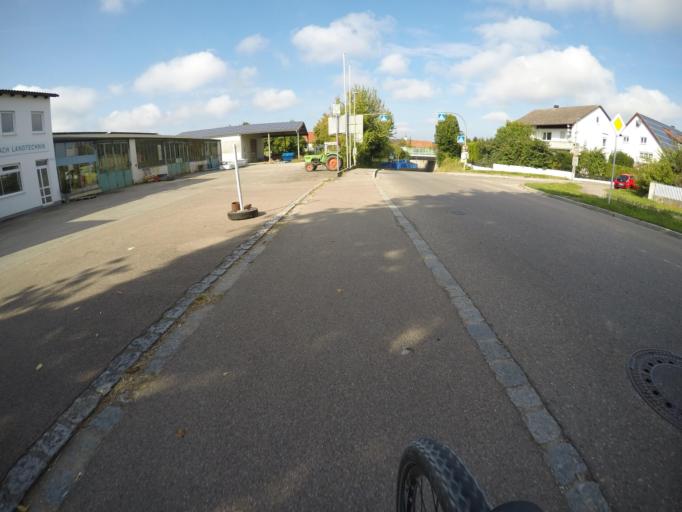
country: DE
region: Bavaria
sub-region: Swabia
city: Westendorf
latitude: 48.5725
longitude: 10.8447
